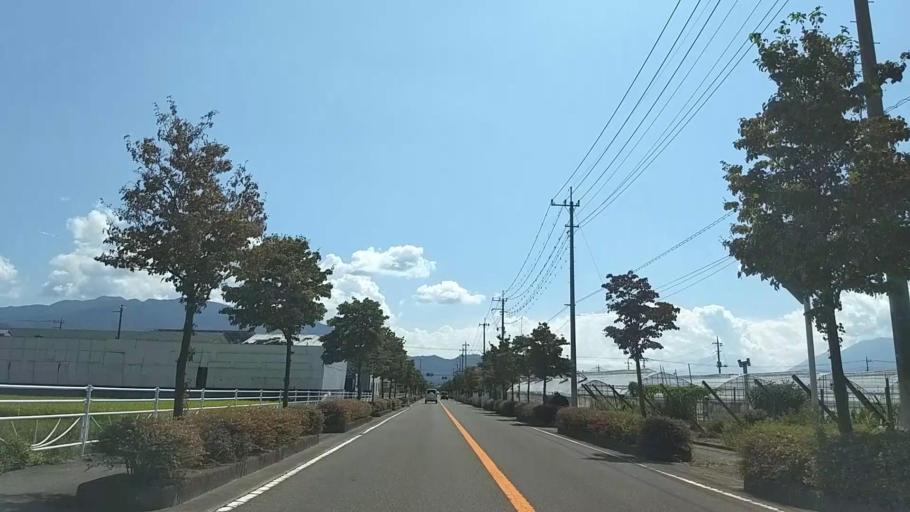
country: JP
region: Yamanashi
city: Ryuo
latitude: 35.6015
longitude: 138.5044
